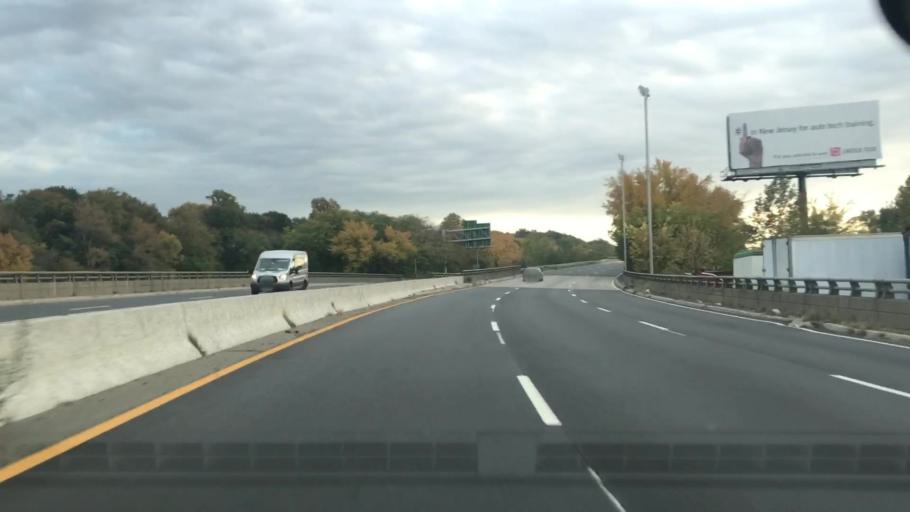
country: US
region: New Jersey
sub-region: Hudson County
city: Kearny
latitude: 40.7805
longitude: -74.1490
